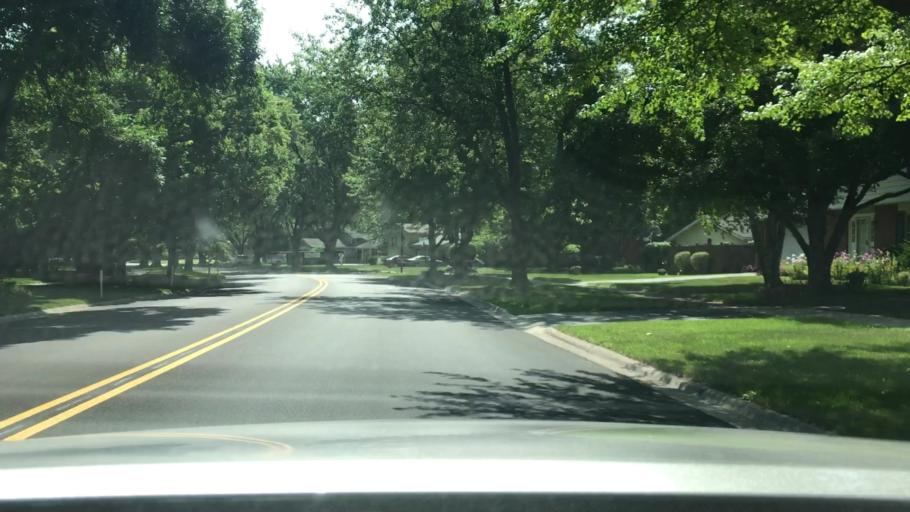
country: US
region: Illinois
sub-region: DuPage County
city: Naperville
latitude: 41.7408
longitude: -88.1316
